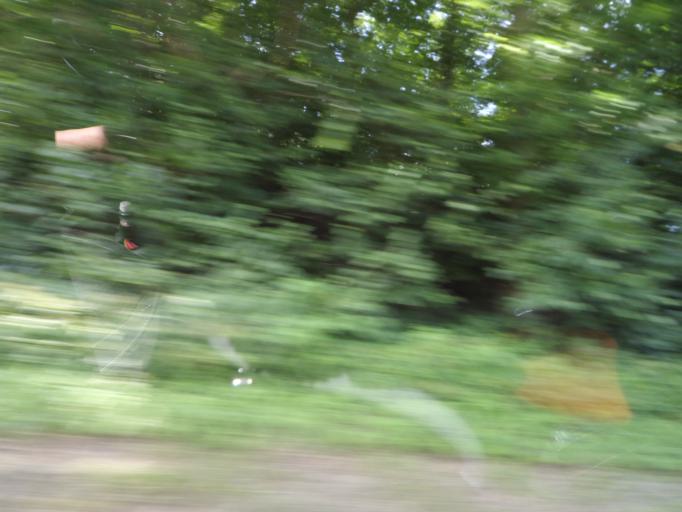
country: DK
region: South Denmark
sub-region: Assens Kommune
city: Arup
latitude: 55.3720
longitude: 10.0359
